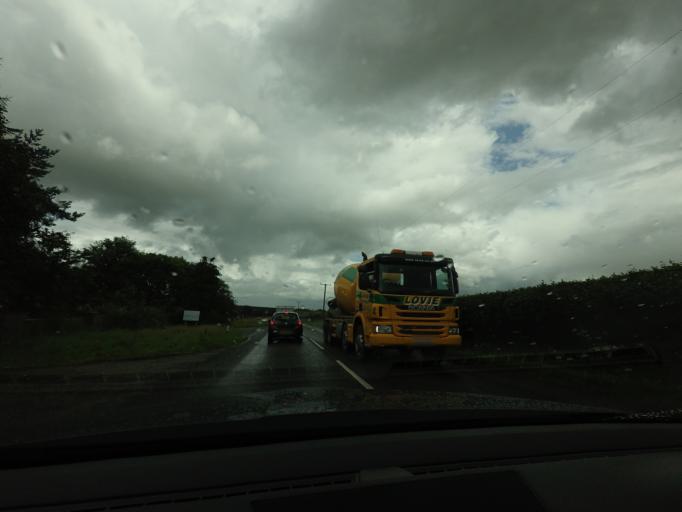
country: GB
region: Scotland
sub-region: Aberdeenshire
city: Turriff
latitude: 57.5498
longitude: -2.4422
